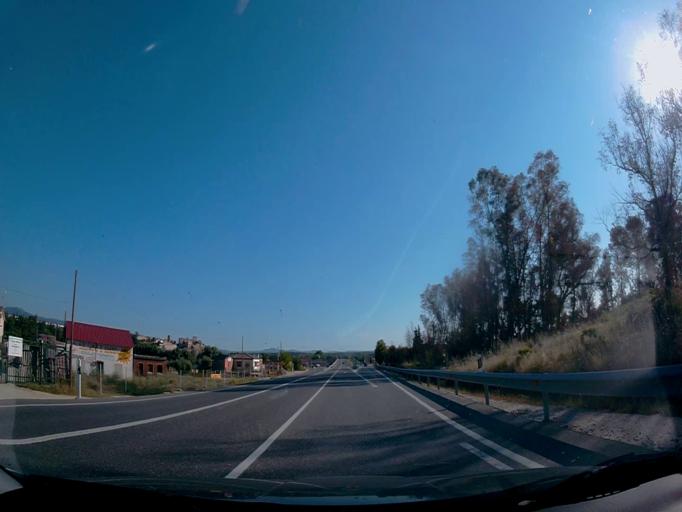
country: ES
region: Castille-La Mancha
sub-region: Province of Toledo
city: Escalona
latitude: 40.1555
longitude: -4.4015
